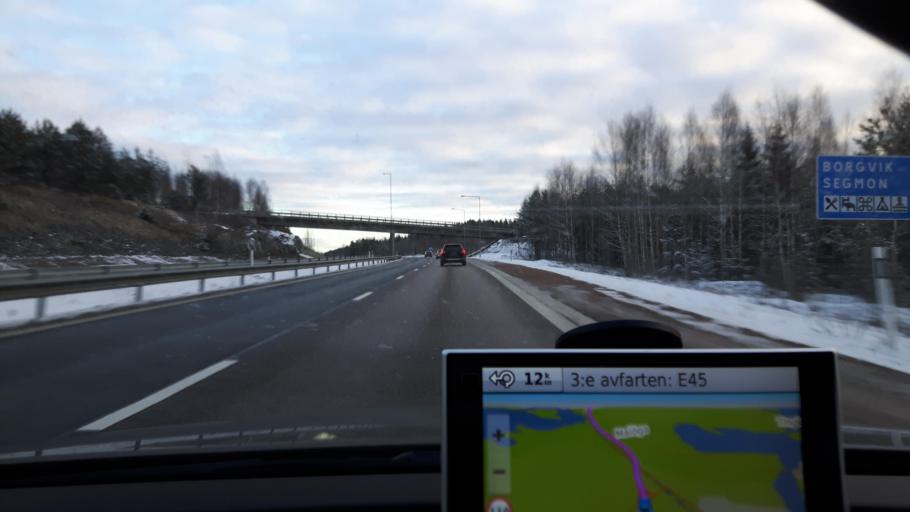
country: SE
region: Vaermland
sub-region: Grums Kommun
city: Slottsbron
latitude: 59.2842
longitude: 13.0391
